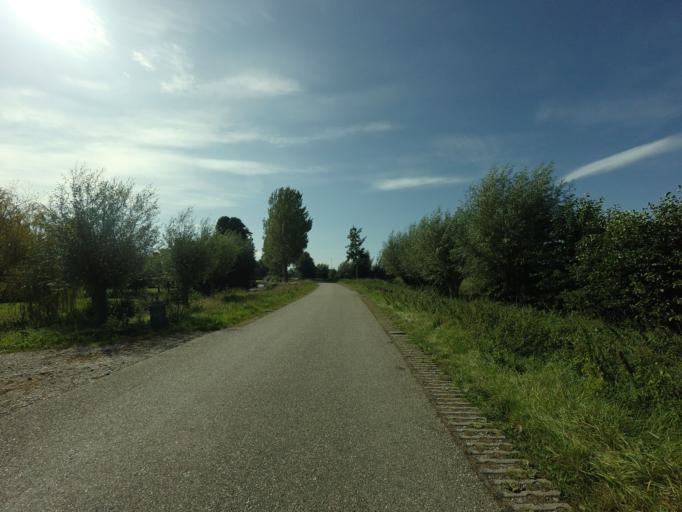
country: NL
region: South Holland
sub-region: Gemeente Gorinchem
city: Gorinchem
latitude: 51.8777
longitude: 5.0241
